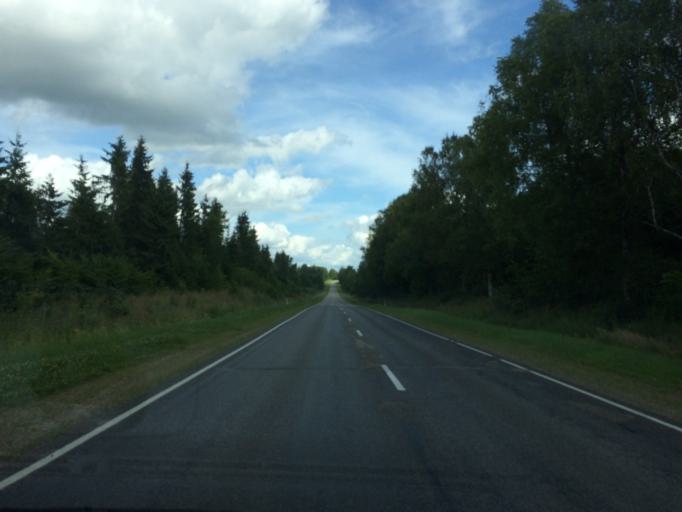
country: LV
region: Rezekne
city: Rezekne
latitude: 56.6206
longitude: 27.4543
